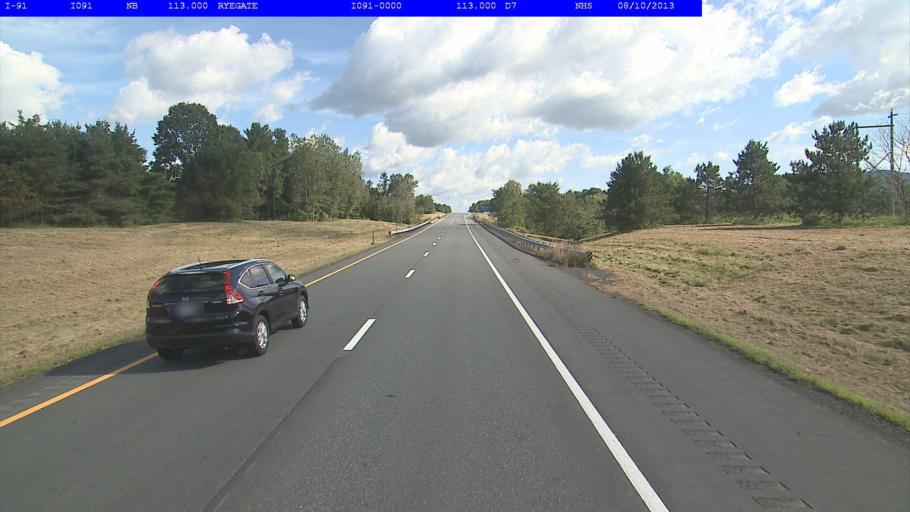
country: US
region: New Hampshire
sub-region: Grafton County
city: Woodsville
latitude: 44.1961
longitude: -72.0716
